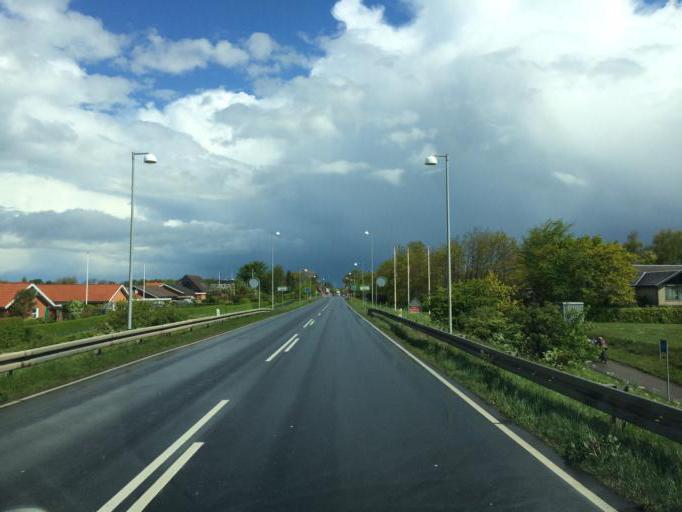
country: DK
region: Central Jutland
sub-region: Holstebro Kommune
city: Vinderup
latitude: 56.4744
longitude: 8.7750
